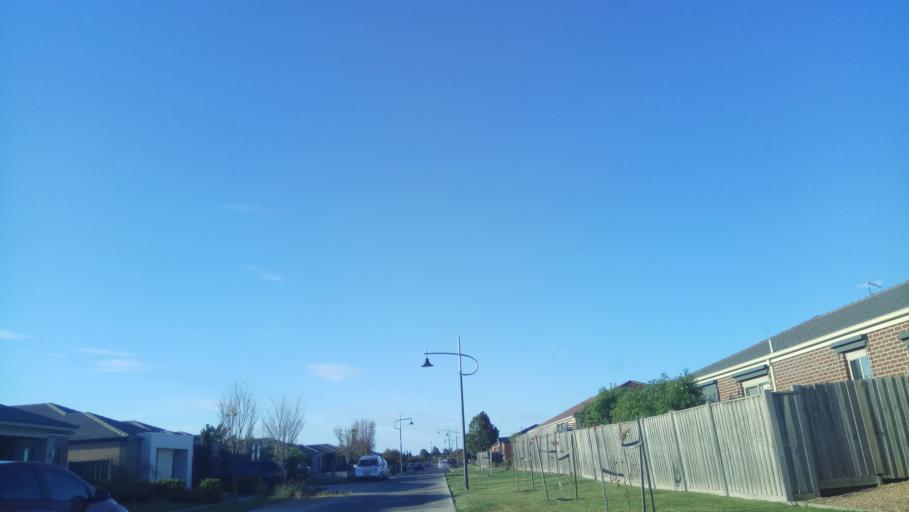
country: AU
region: Victoria
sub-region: Wyndham
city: Point Cook
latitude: -37.9097
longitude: 144.7351
